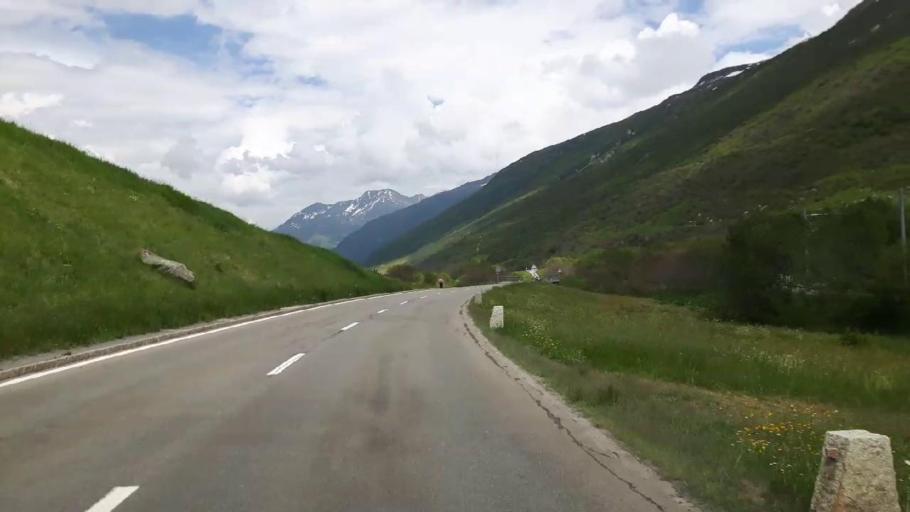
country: CH
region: Uri
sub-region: Uri
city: Andermatt
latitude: 46.6008
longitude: 8.5057
